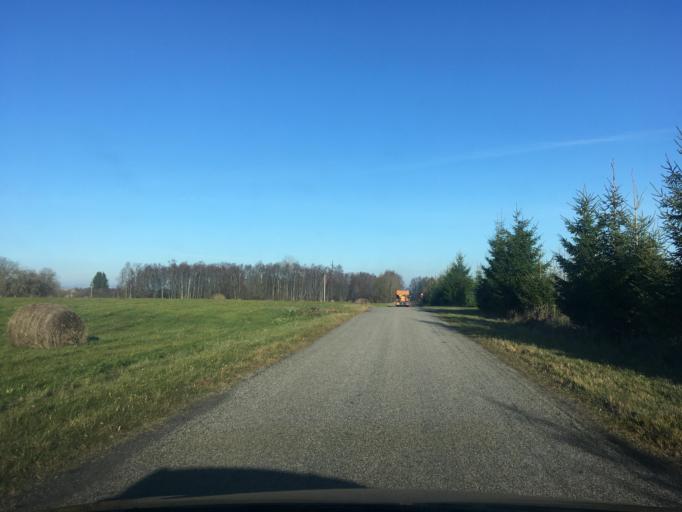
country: EE
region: Harju
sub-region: Maardu linn
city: Maardu
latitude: 59.4722
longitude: 25.1158
